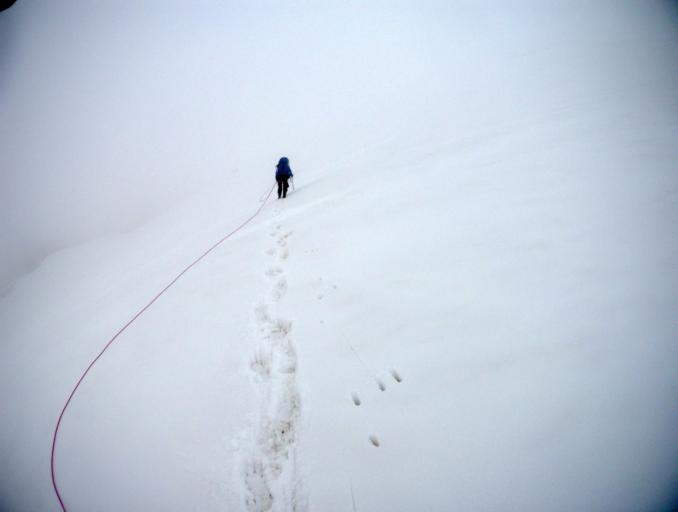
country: RU
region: Kabardino-Balkariya
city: Terskol
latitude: 43.3797
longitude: 42.4705
